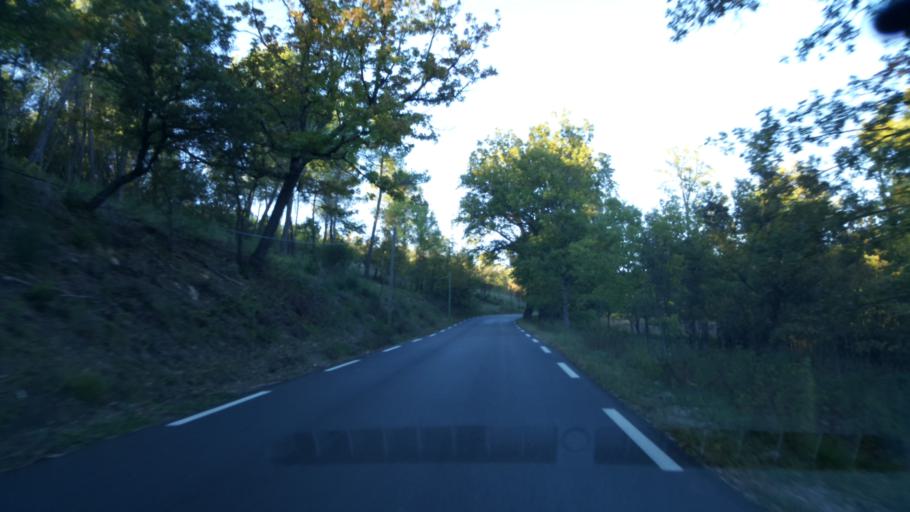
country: FR
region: Provence-Alpes-Cote d'Azur
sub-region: Departement du Var
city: Barjols
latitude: 43.5562
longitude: 5.9546
